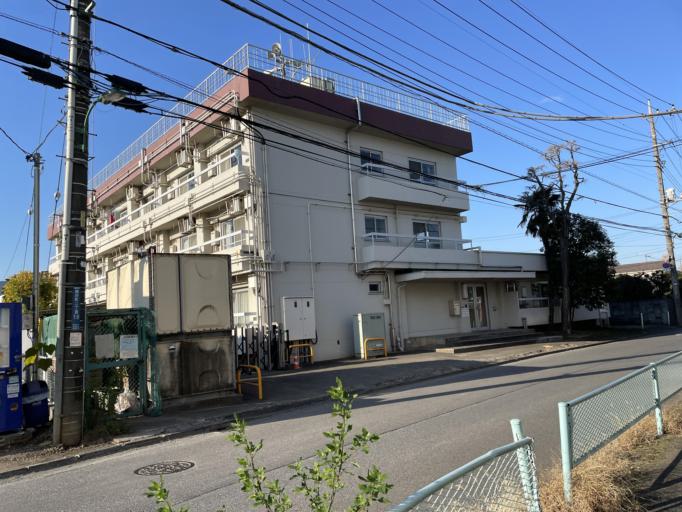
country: JP
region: Saitama
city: Asaka
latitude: 35.7885
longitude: 139.5820
